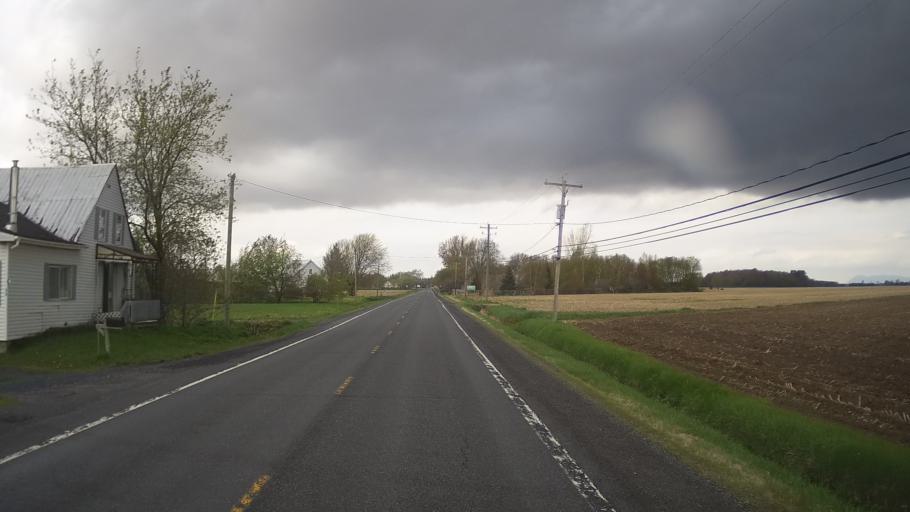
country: CA
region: Quebec
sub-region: Monteregie
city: Rougemont
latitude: 45.3446
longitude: -73.0959
